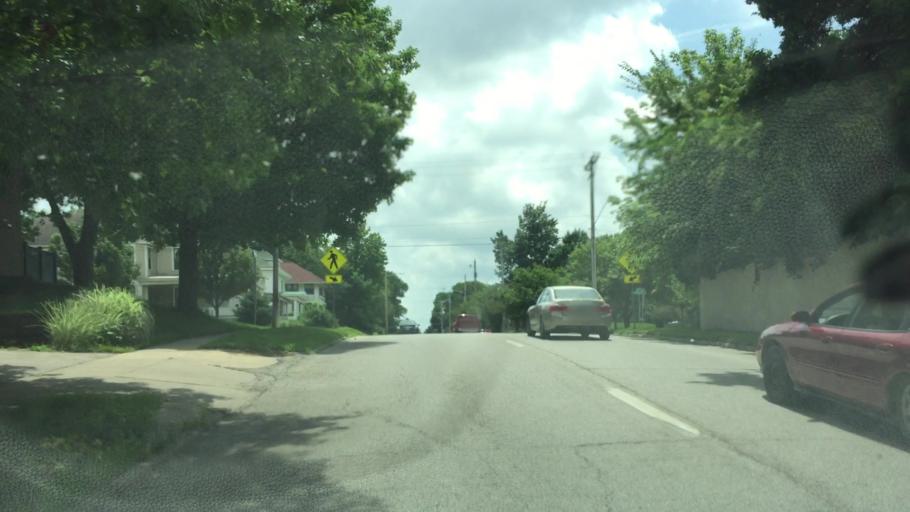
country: US
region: Iowa
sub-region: Johnson County
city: Iowa City
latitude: 41.6604
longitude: -91.5258
